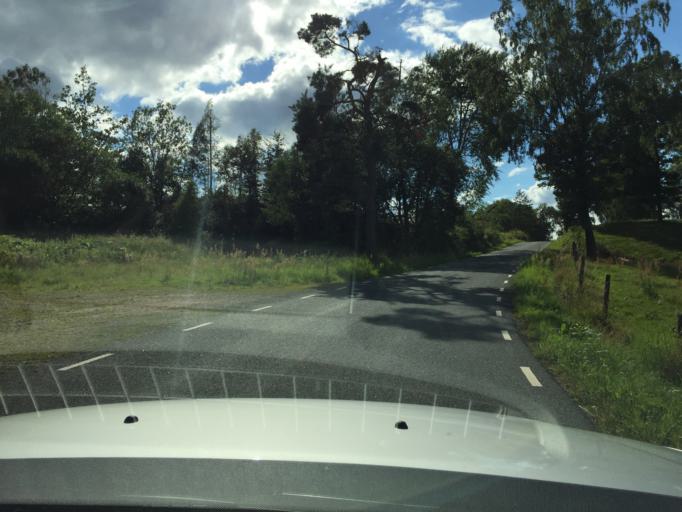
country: SE
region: Skane
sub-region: Hassleholms Kommun
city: Sosdala
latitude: 56.0013
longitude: 13.7779
